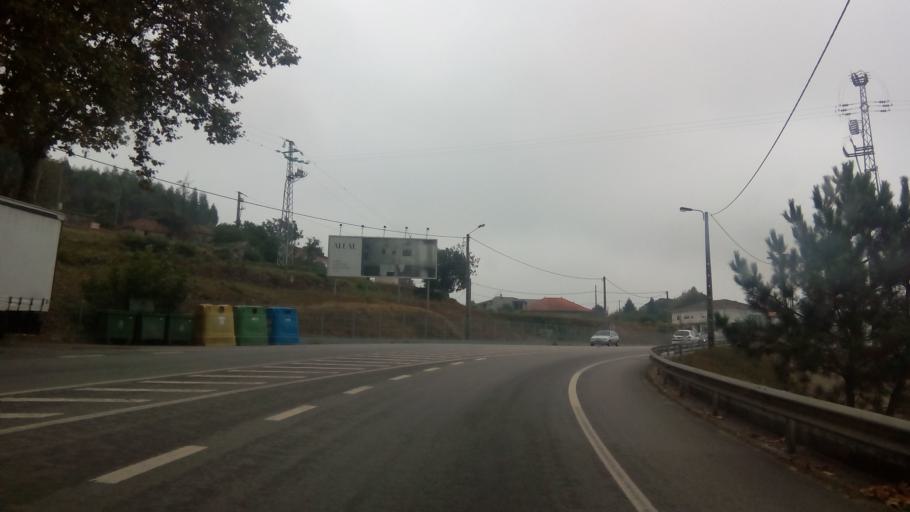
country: PT
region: Porto
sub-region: Paredes
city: Gandra
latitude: 41.1938
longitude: -8.4073
